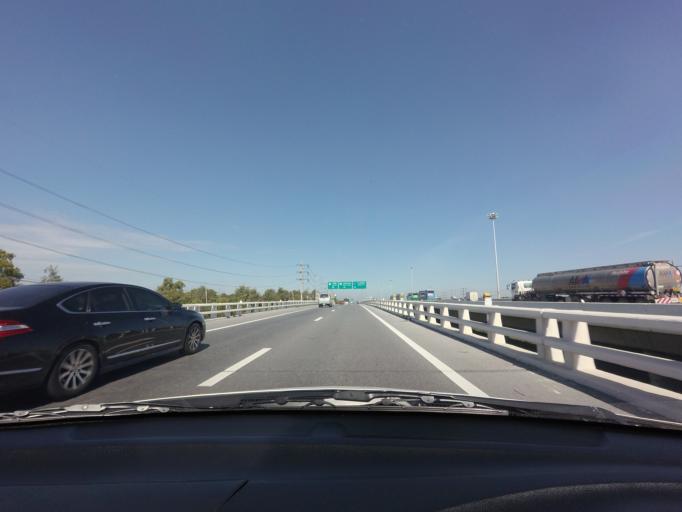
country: TH
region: Pathum Thani
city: Thanyaburi
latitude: 14.0004
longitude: 100.7079
